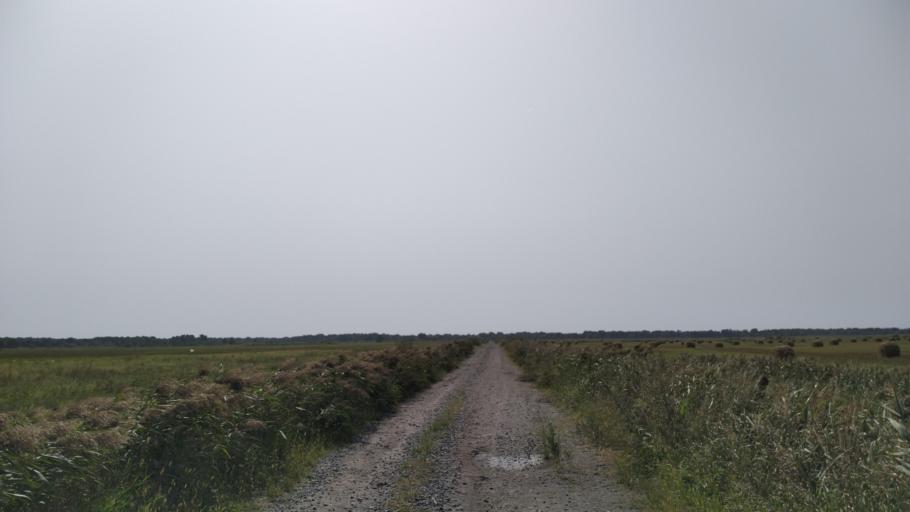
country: BY
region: Brest
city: Davyd-Haradok
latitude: 51.9810
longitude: 27.1749
